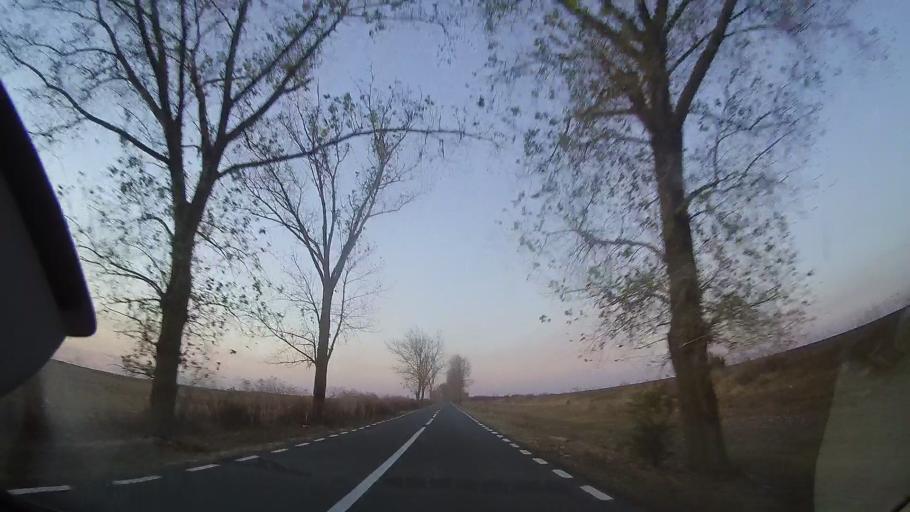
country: RO
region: Constanta
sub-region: Comuna Cobadin
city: Cobadin
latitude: 44.0399
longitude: 28.2572
